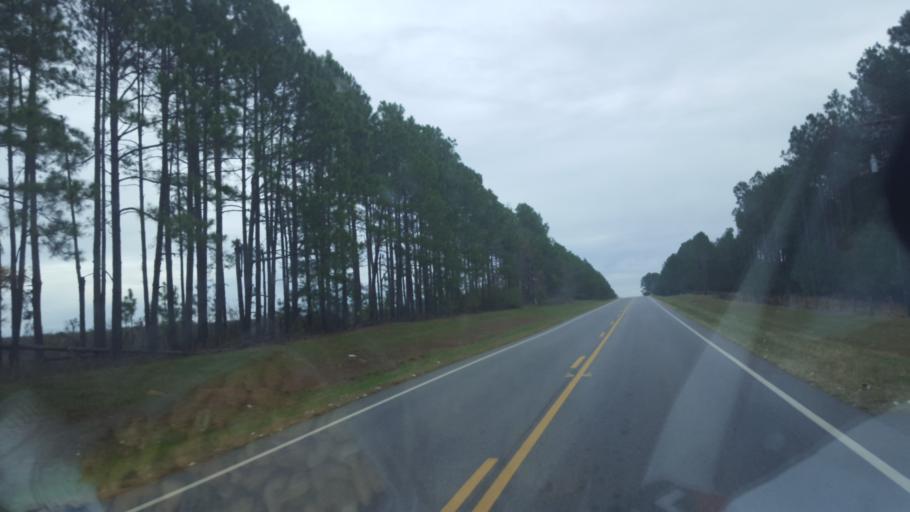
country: US
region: Georgia
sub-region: Turner County
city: Ashburn
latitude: 31.7160
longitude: -83.6171
